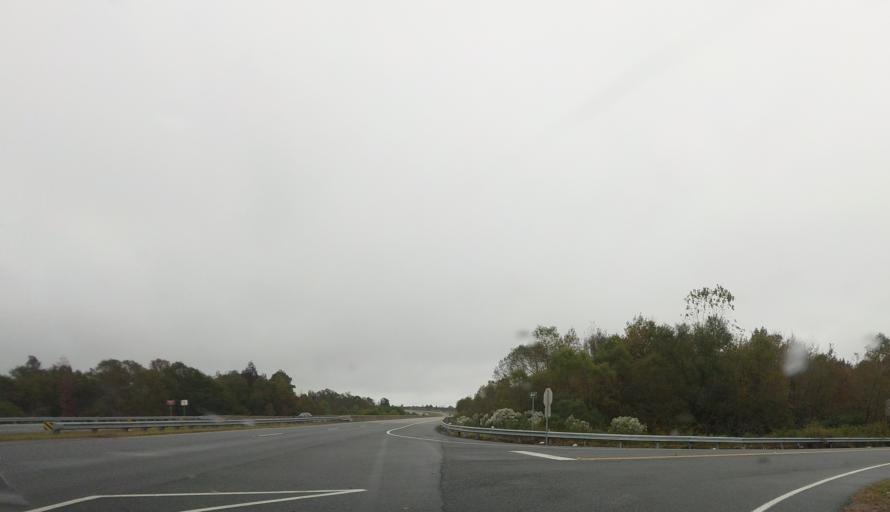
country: US
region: Georgia
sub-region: Taylor County
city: Reynolds
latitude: 32.5459
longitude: -84.0008
